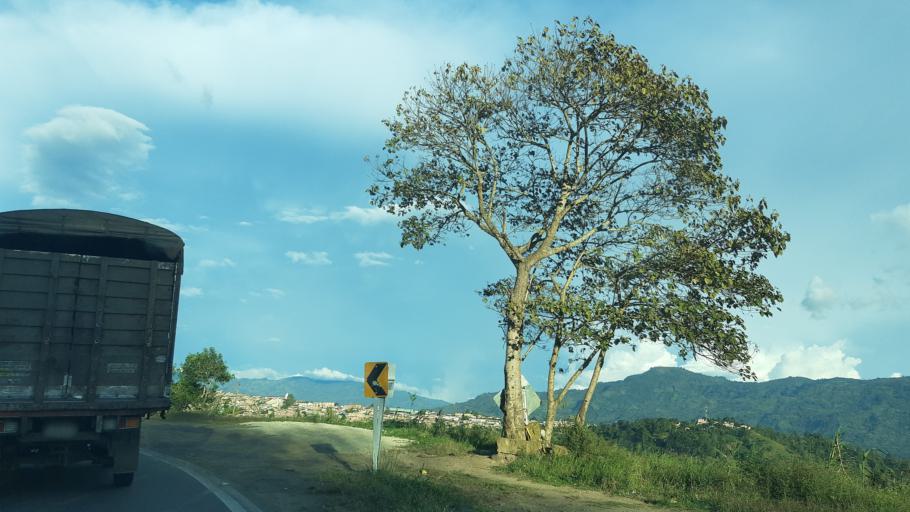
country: CO
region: Boyaca
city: Guateque
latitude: 5.0049
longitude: -73.4886
